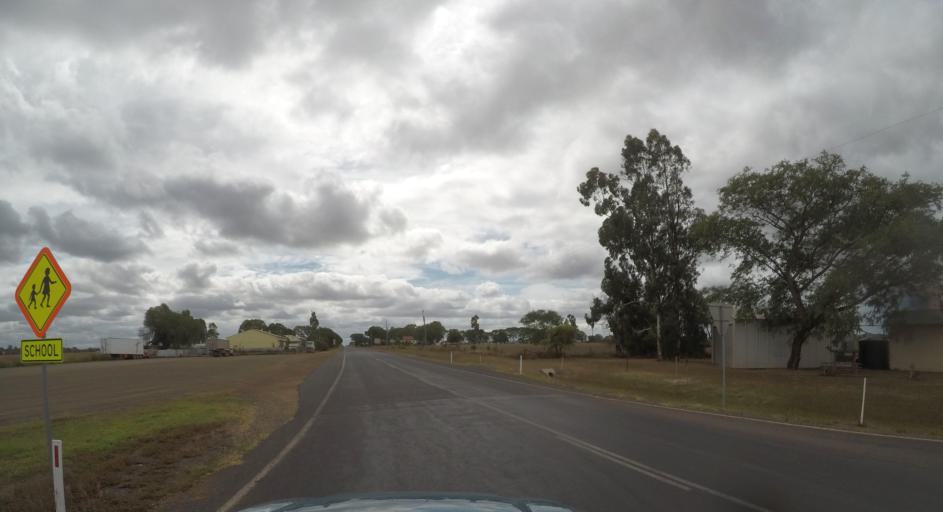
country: AU
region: Queensland
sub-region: South Burnett
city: Kingaroy
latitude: -26.3950
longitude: 151.2435
